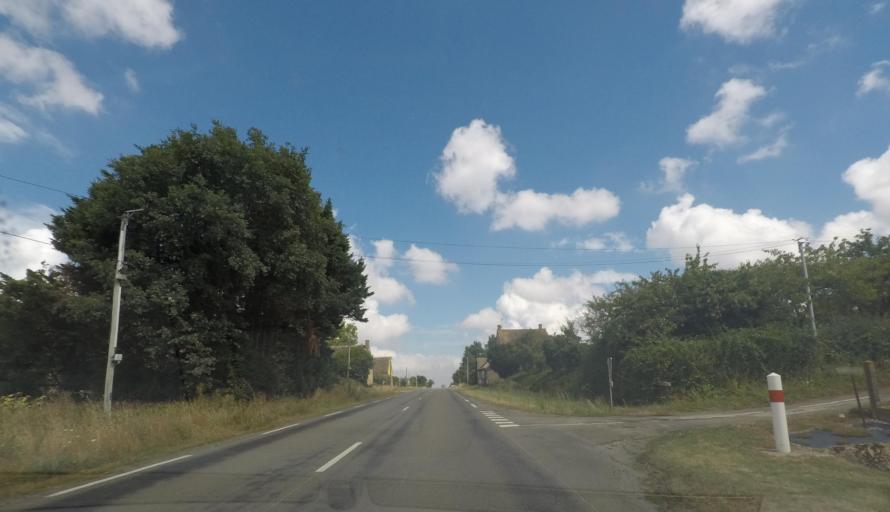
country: FR
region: Pays de la Loire
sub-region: Departement de la Sarthe
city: Saint-Cosme-en-Vairais
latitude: 48.2424
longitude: 0.4408
